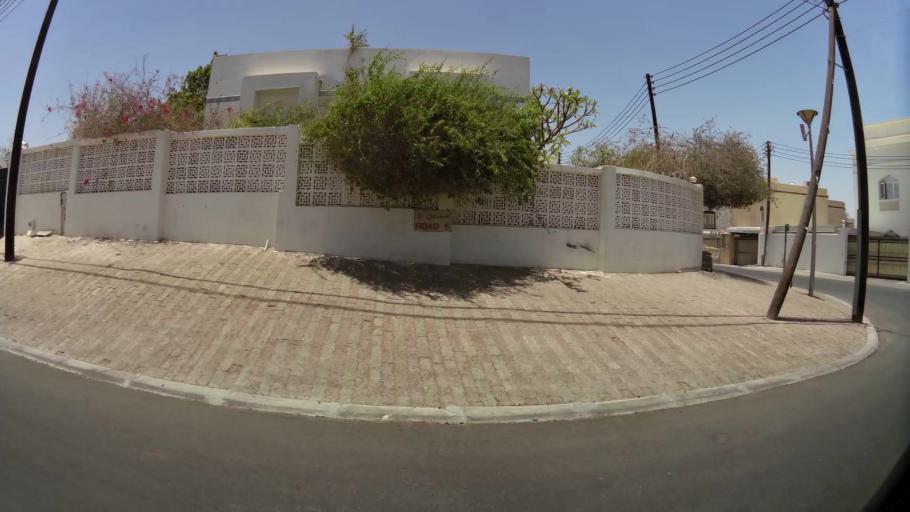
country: OM
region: Muhafazat Masqat
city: Bawshar
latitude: 23.5996
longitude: 58.4528
